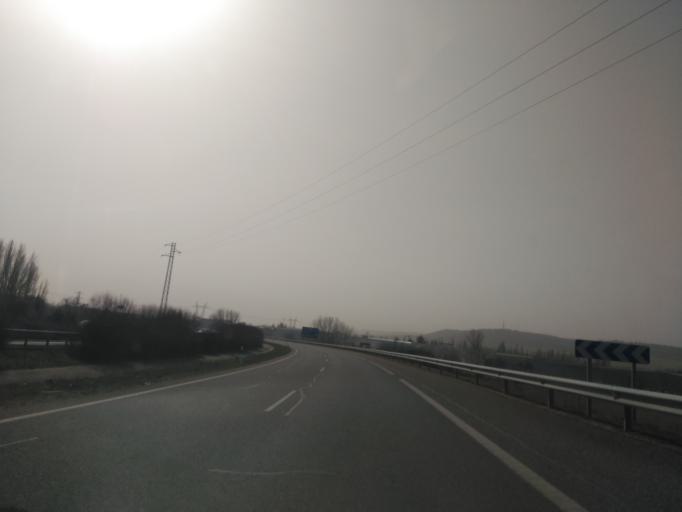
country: ES
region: Castille and Leon
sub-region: Provincia de Palencia
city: Villamuriel de Cerrato
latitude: 41.9689
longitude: -4.5041
